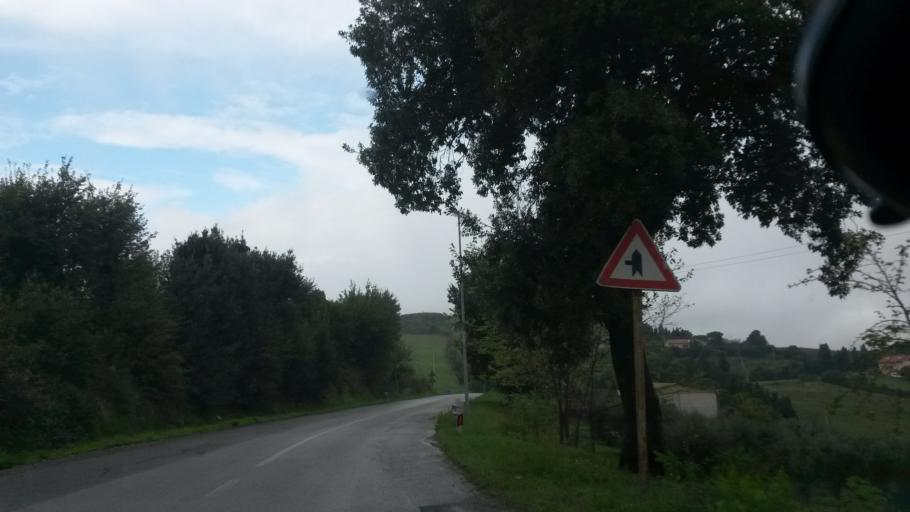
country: IT
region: Tuscany
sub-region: Provincia di Livorno
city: Rosignano Marittimo
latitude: 43.4181
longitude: 10.4600
